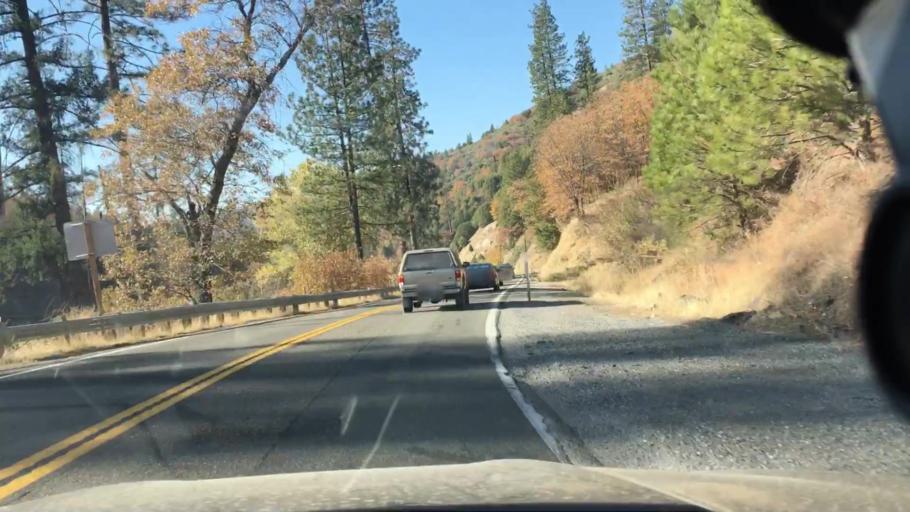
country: US
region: California
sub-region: El Dorado County
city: Pollock Pines
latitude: 38.7728
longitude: -120.3899
